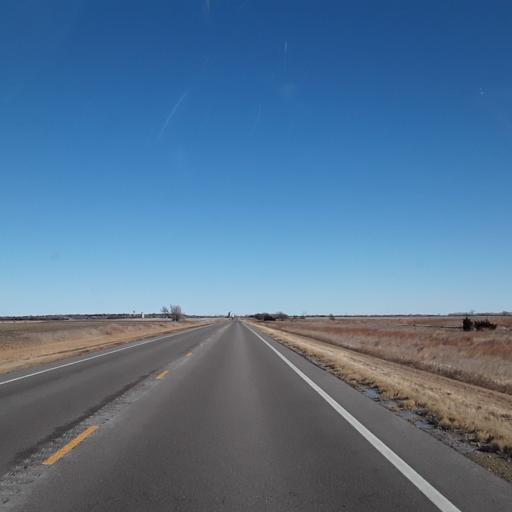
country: US
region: Kansas
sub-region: Pawnee County
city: Larned
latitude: 38.1419
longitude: -99.1476
